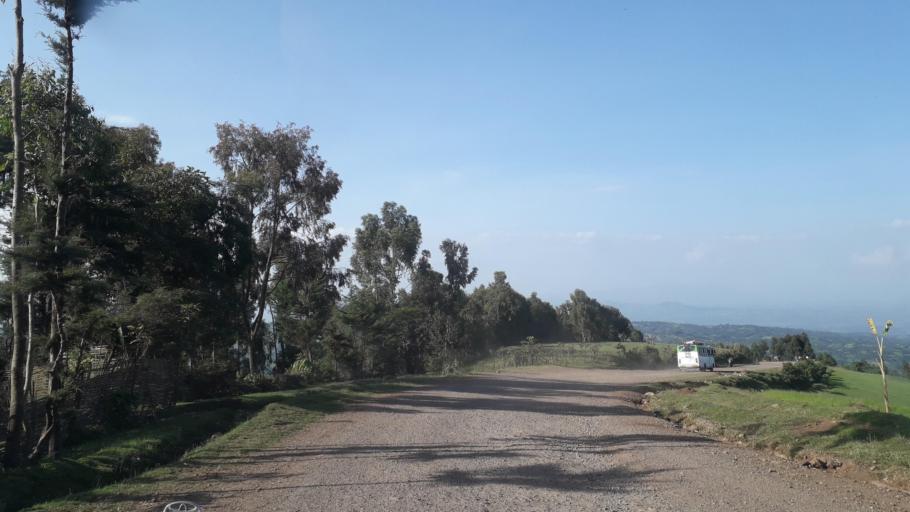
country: ET
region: Oromiya
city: Jima
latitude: 7.4564
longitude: 36.8707
